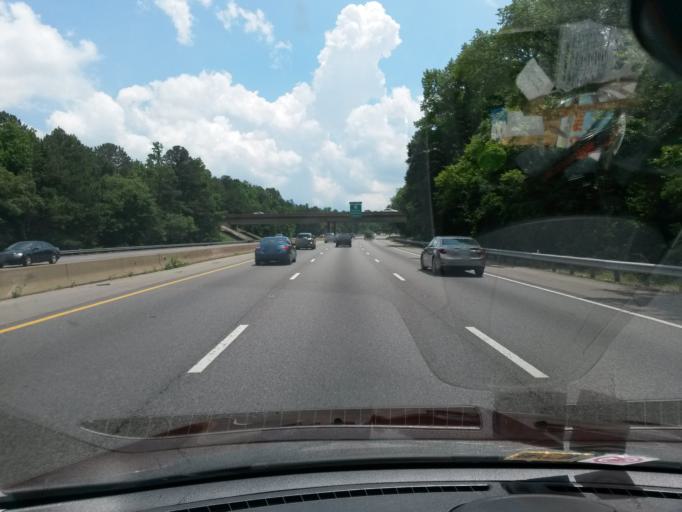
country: US
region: Virginia
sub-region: Chesterfield County
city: Chester
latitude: 37.3788
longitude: -77.4100
